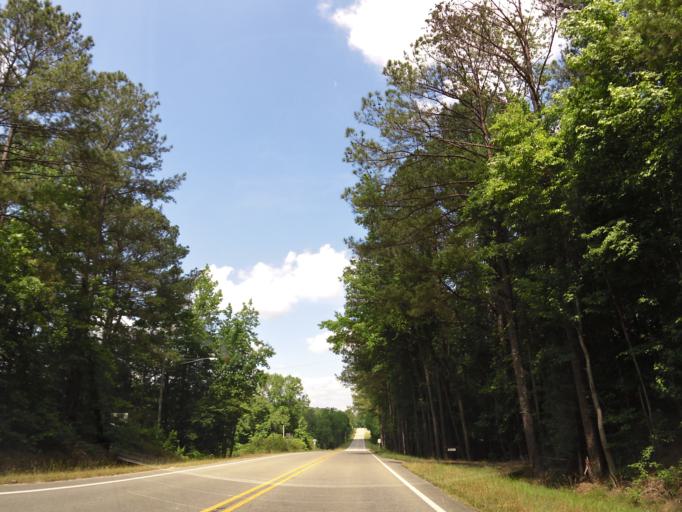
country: US
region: Alabama
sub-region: Marion County
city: Guin
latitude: 33.9548
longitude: -87.9333
